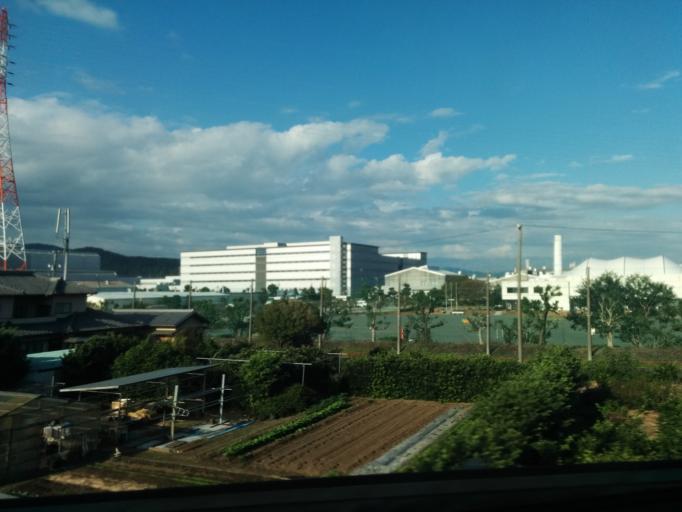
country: JP
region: Shizuoka
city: Kosai-shi
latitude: 34.7157
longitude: 137.4807
